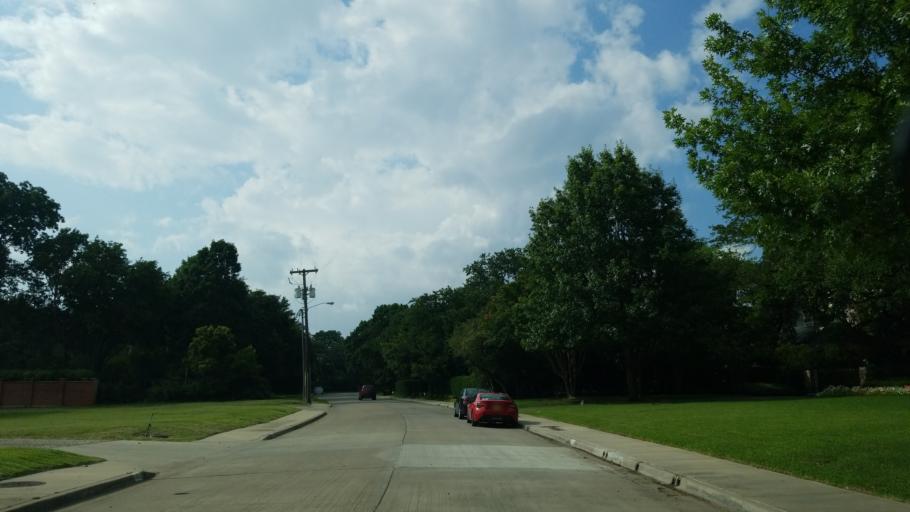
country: US
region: Texas
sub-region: Dallas County
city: University Park
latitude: 32.8482
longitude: -96.7977
